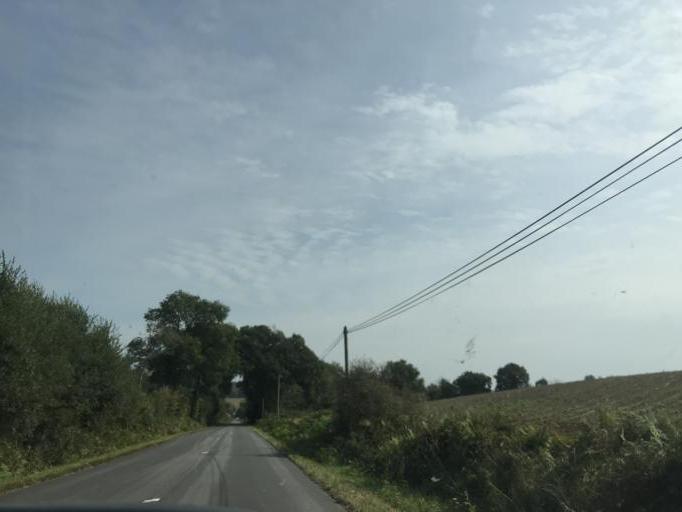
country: FR
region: Brittany
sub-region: Departement du Finistere
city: Loperec
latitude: 48.2956
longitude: -4.0098
